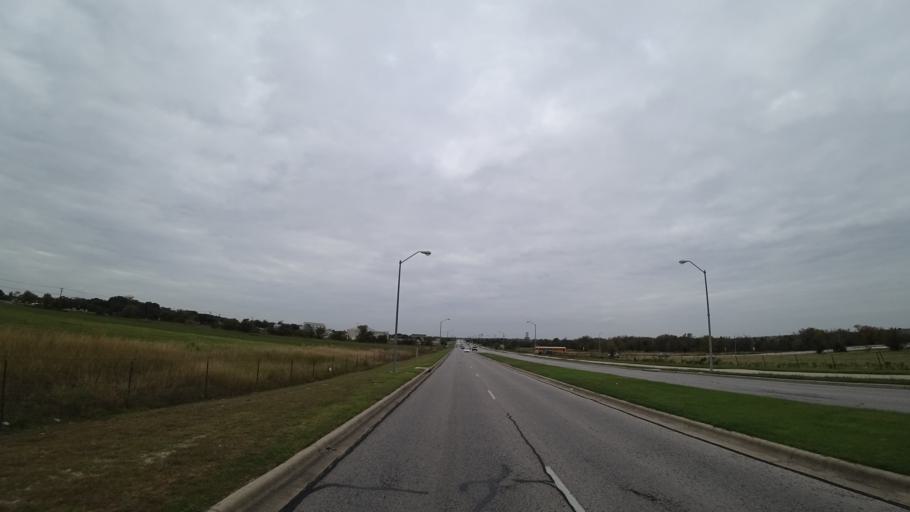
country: US
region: Texas
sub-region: Travis County
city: Pflugerville
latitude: 30.4563
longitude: -97.6103
